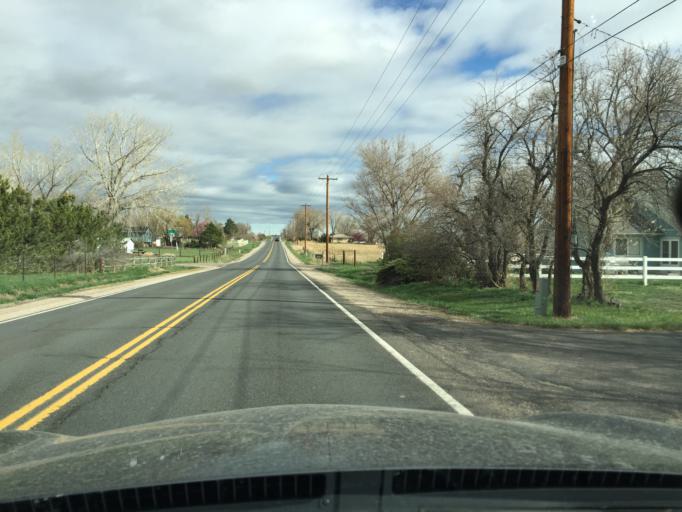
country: US
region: Colorado
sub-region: Adams County
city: Northglenn
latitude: 39.9750
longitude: -104.9972
